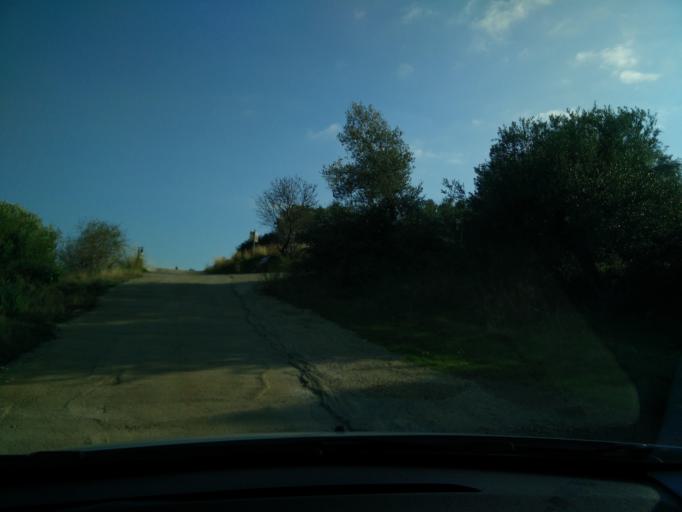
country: GR
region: Crete
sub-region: Nomos Lasithiou
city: Gra Liyia
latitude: 35.0268
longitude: 25.5682
